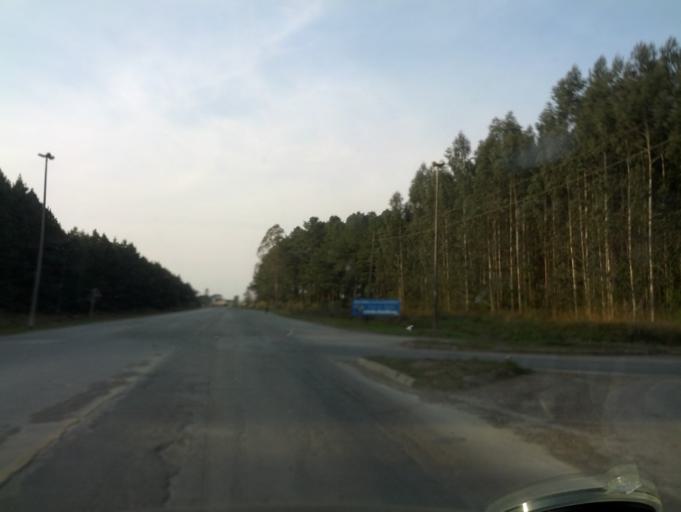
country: BR
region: Santa Catarina
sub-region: Otacilio Costa
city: Otacilio Costa
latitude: -27.5118
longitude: -50.1309
